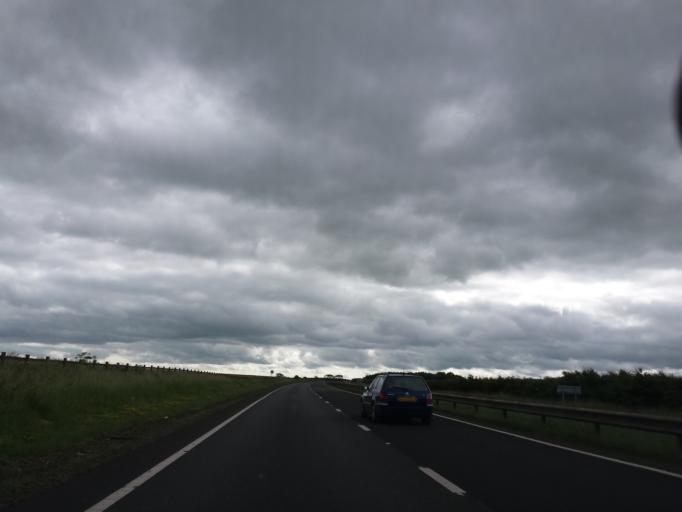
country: GB
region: Scotland
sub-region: East Lothian
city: Tranent
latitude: 55.9516
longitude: -2.9318
